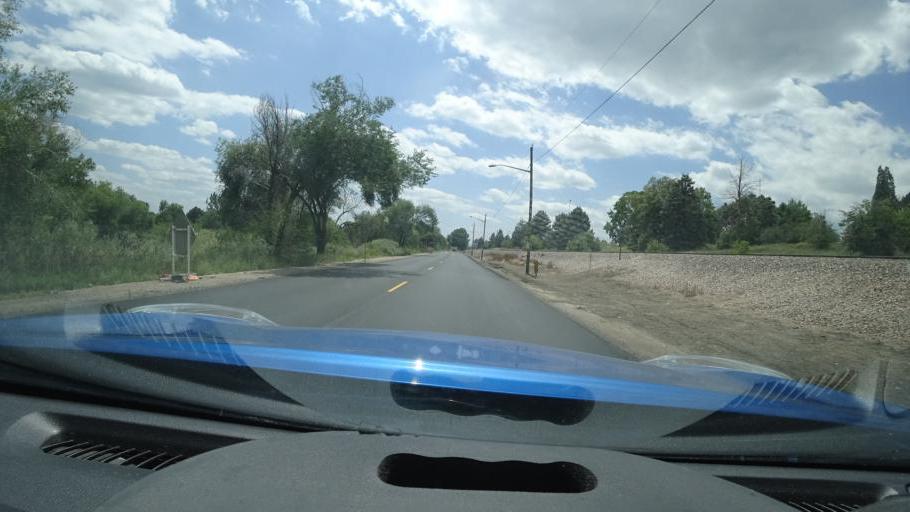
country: US
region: Colorado
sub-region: Arapahoe County
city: Englewood
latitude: 39.6870
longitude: -105.0009
